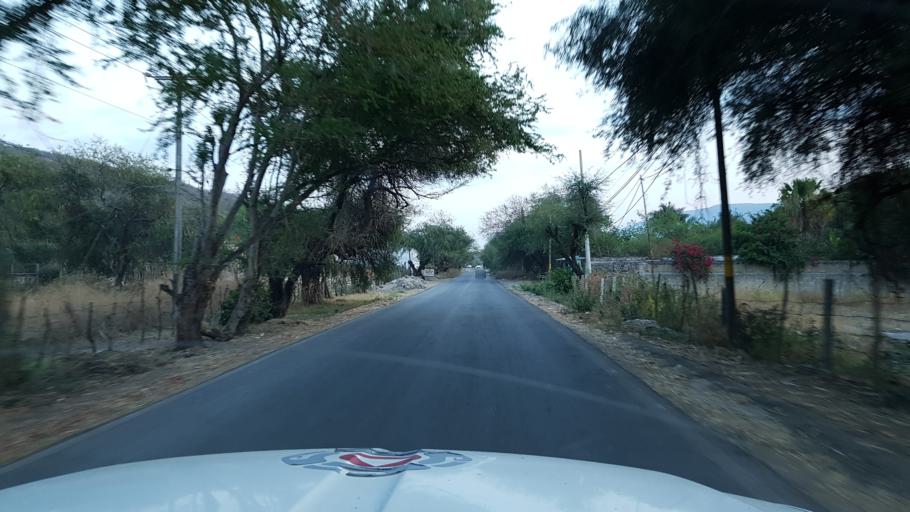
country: MX
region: Morelos
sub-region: Tlaltizapan de Zapata
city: Colonia Palo Prieto (Chipitongo)
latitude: 18.7095
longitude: -99.1075
